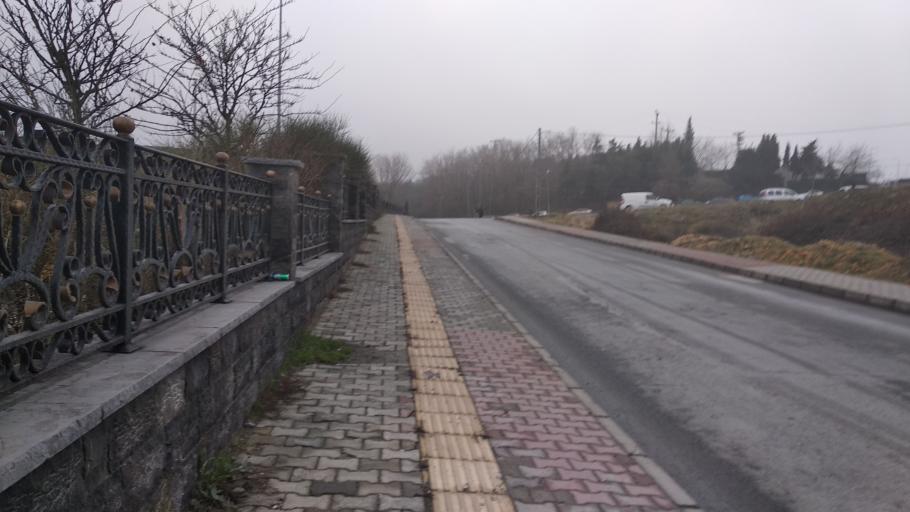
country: TR
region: Istanbul
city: Basaksehir
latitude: 41.1794
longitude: 28.7477
